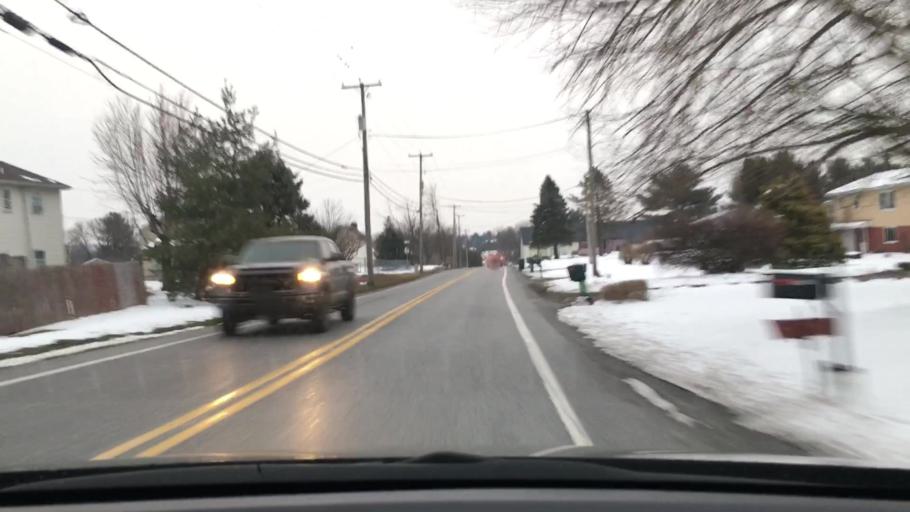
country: US
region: Pennsylvania
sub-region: York County
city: Weigelstown
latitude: 39.9627
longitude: -76.8401
